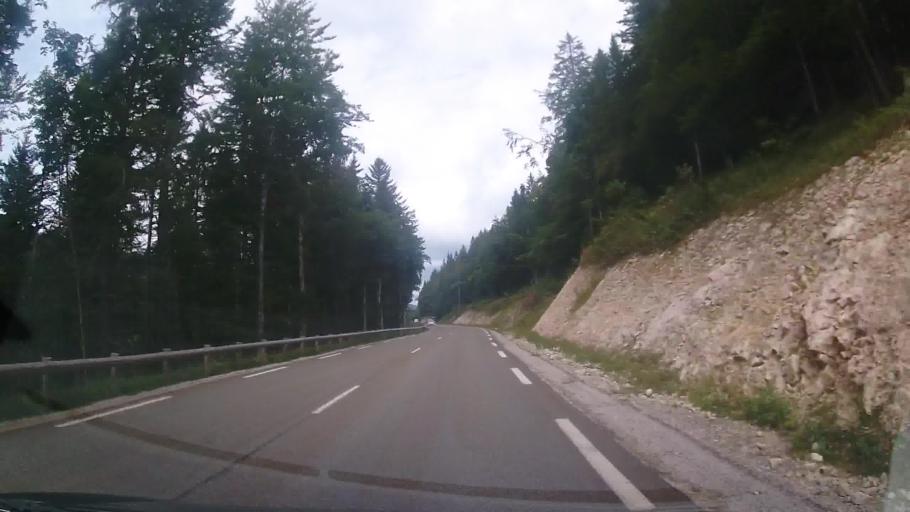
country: FR
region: Franche-Comte
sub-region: Departement du Jura
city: Les Rousses
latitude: 46.4244
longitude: 6.0681
